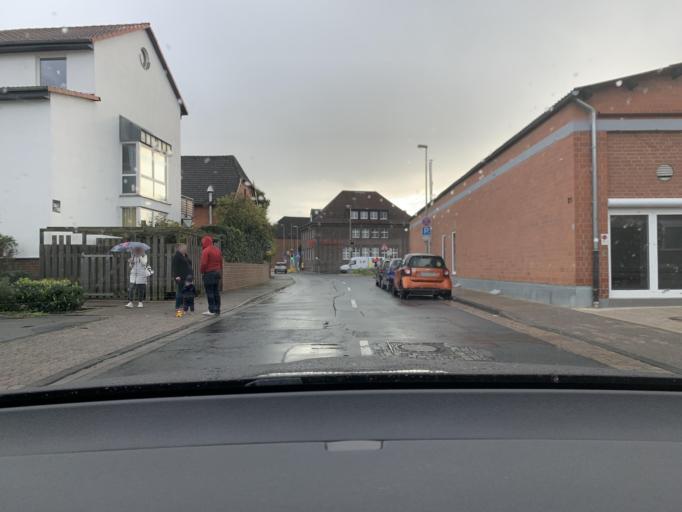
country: DE
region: Lower Saxony
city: Laatzen
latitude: 52.3619
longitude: 9.8592
